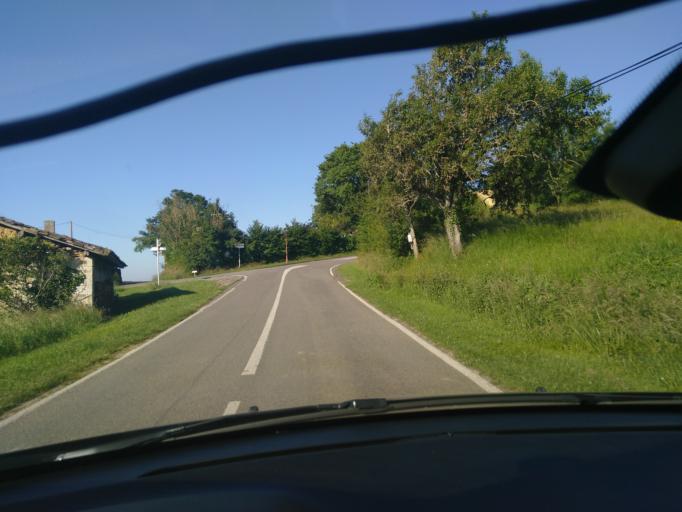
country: FR
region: Midi-Pyrenees
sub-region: Departement du Tarn-et-Garonne
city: Beaumont-de-Lomagne
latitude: 43.7807
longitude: 0.9931
